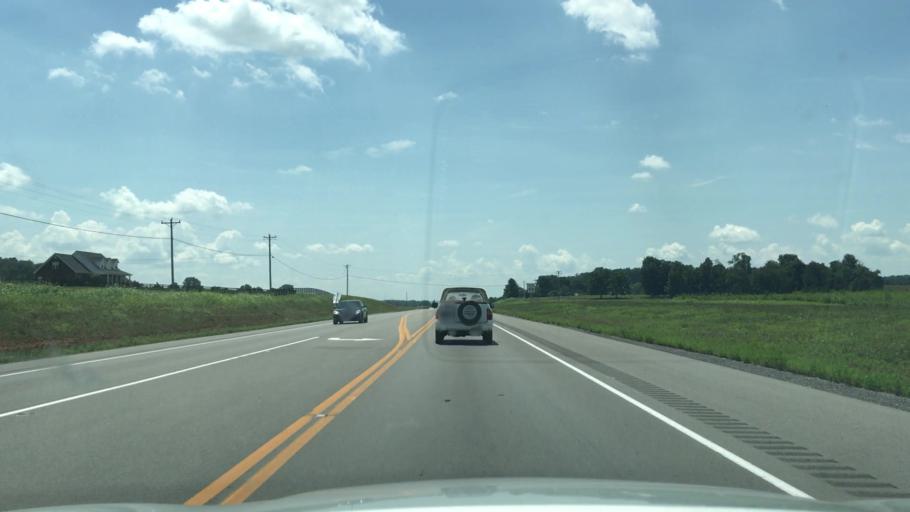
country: US
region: Kentucky
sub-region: Clinton County
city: Albany
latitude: 36.6418
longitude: -85.1021
